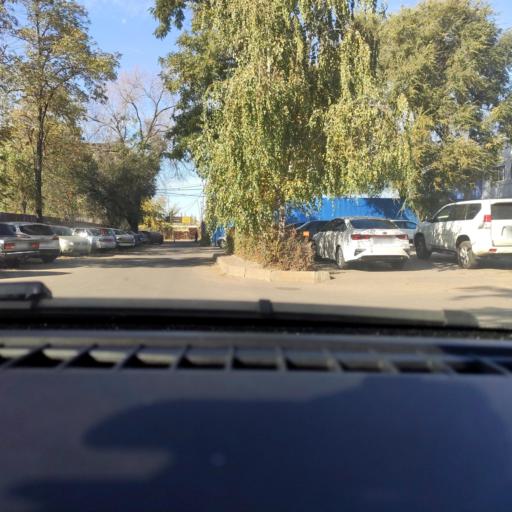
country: RU
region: Voronezj
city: Voronezh
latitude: 51.6525
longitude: 39.2884
